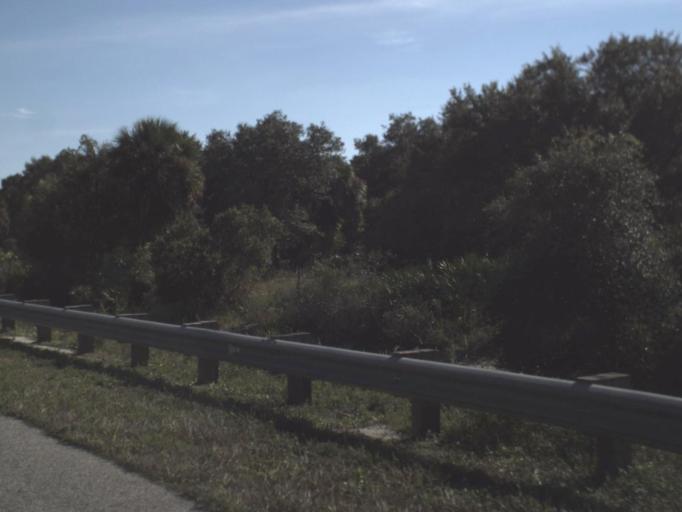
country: US
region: Florida
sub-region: Glades County
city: Moore Haven
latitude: 26.8872
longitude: -81.2328
